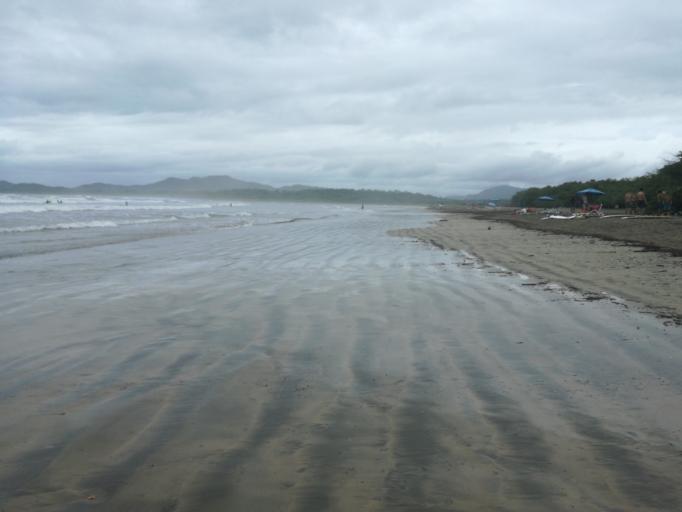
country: CR
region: Guanacaste
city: Santa Cruz
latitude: 10.3032
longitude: -85.8402
